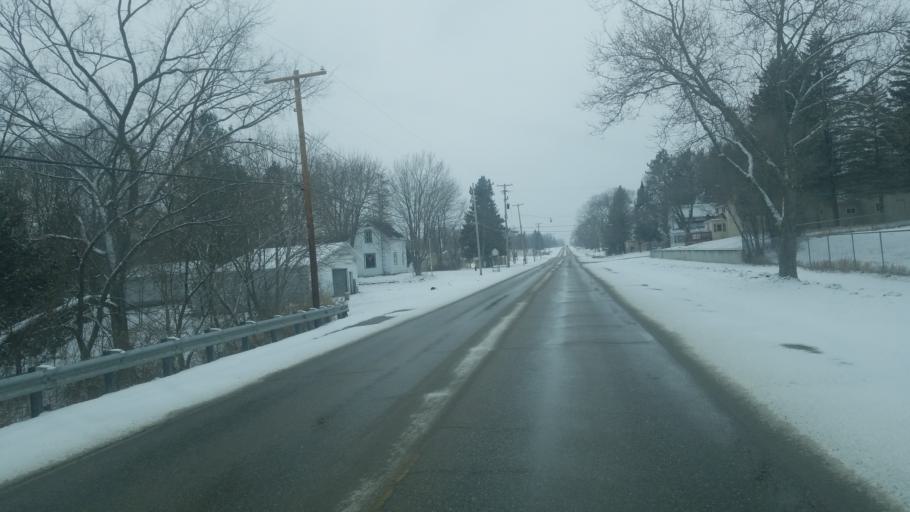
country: US
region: Michigan
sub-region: Osceola County
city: Evart
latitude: 44.1025
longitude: -85.1545
